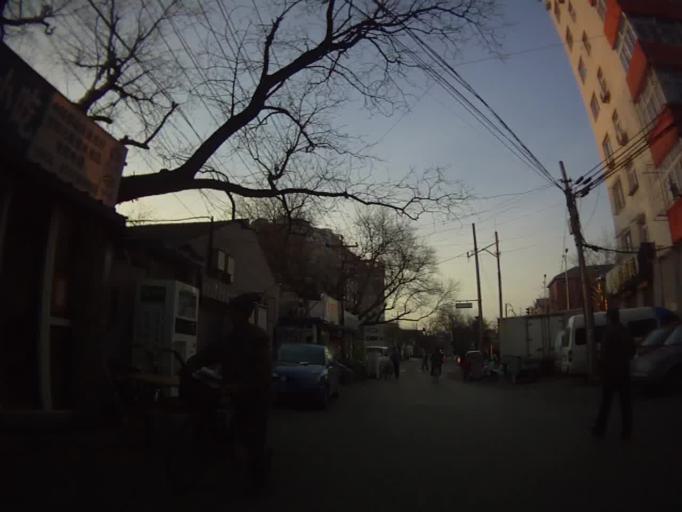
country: CN
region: Beijing
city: Longtan
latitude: 39.8822
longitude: 116.4254
